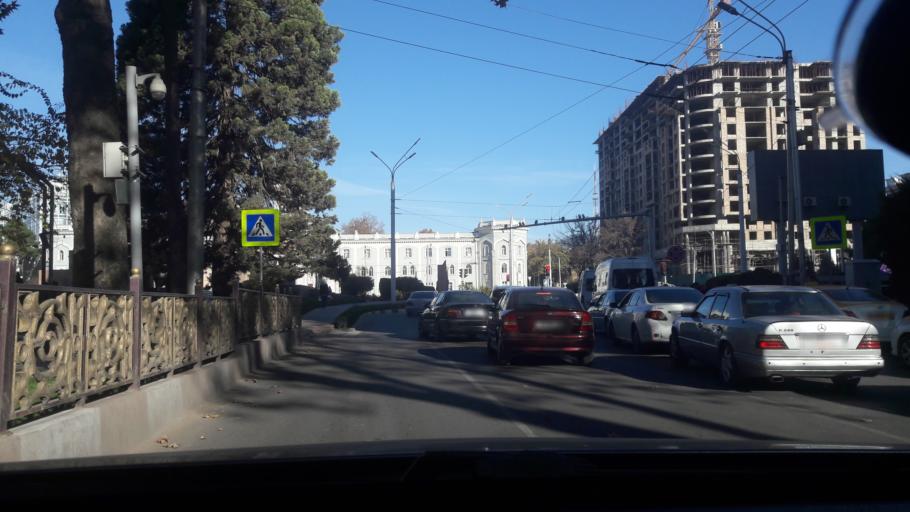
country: TJ
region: Dushanbe
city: Dushanbe
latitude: 38.5618
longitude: 68.7994
